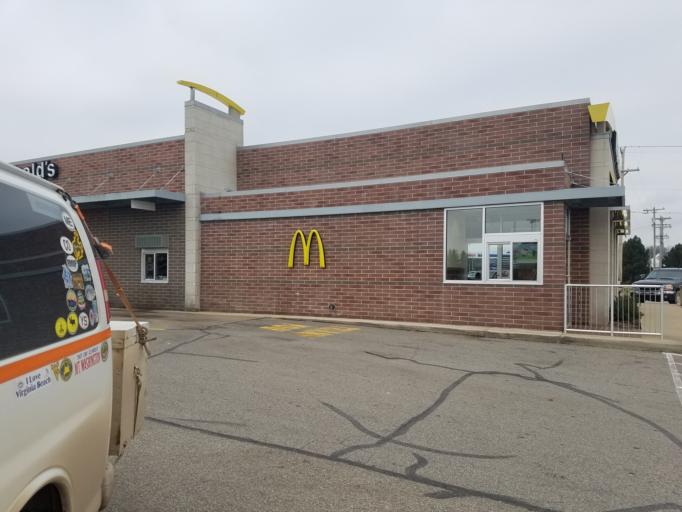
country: US
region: Michigan
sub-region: Wexford County
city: Cadillac
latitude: 44.2808
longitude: -85.4052
